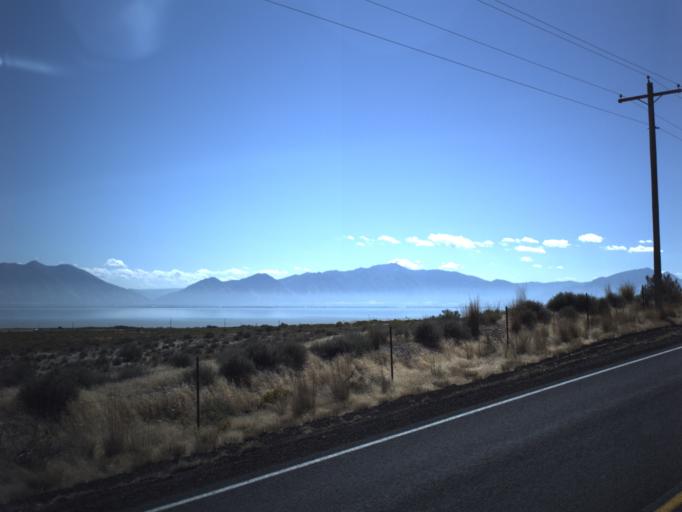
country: US
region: Utah
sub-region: Utah County
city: Saratoga Springs
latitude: 40.2737
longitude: -111.8669
